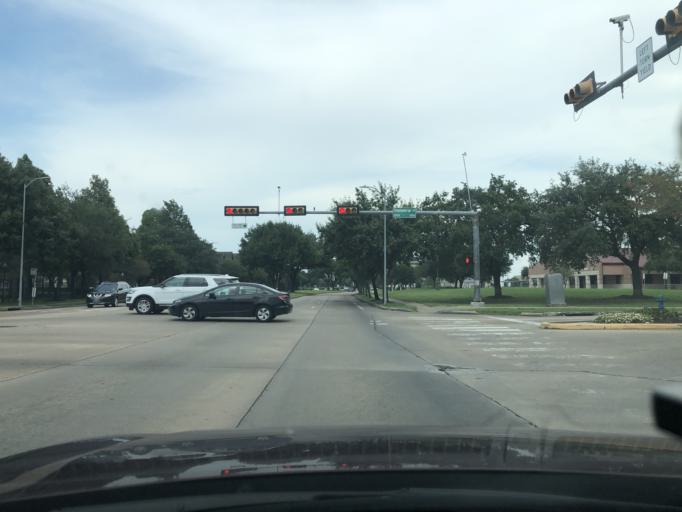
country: US
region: Texas
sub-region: Fort Bend County
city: Mission Bend
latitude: 29.7297
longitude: -95.6000
